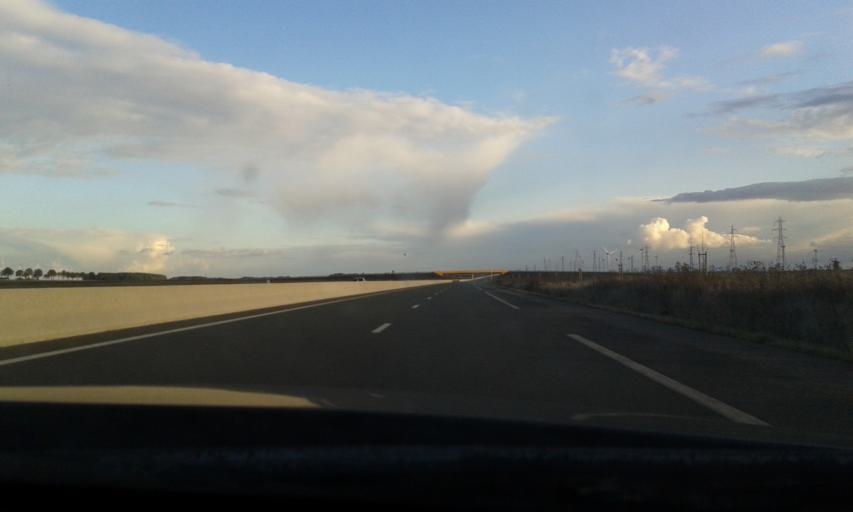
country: FR
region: Centre
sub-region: Departement d'Eure-et-Loir
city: Sours
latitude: 48.3511
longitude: 1.6211
